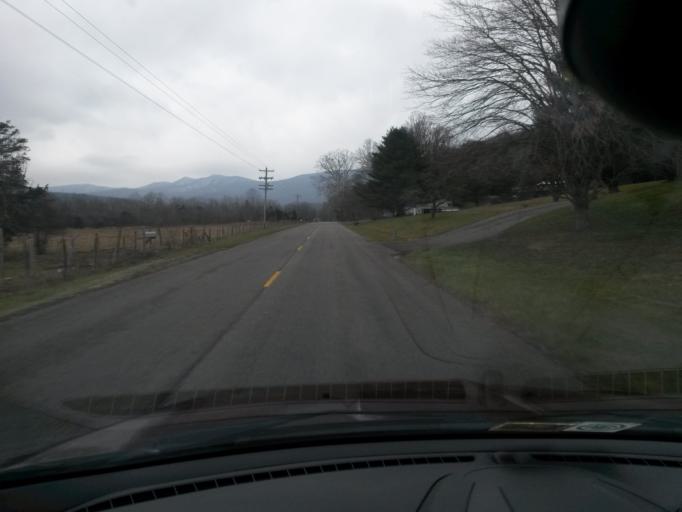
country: US
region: Virginia
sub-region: City of Lexington
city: Lexington
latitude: 37.8654
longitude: -79.5293
